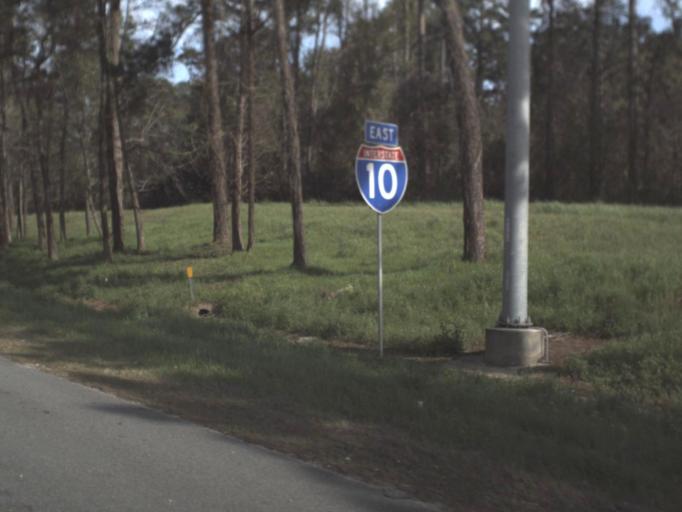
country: US
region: Florida
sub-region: Leon County
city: Tallahassee
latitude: 30.4857
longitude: -84.2973
